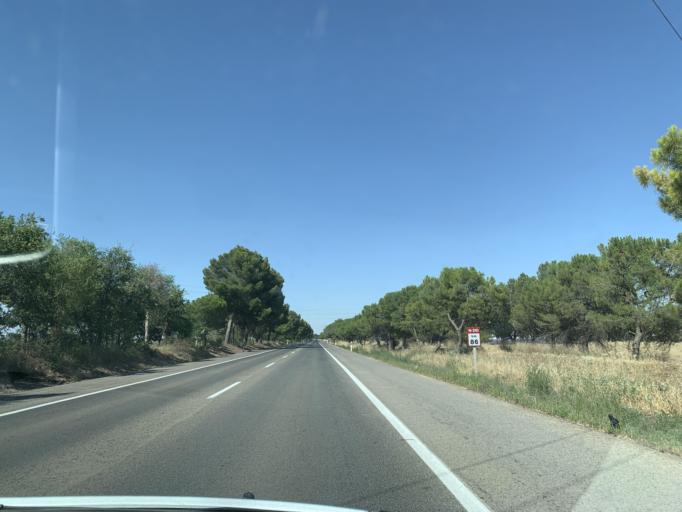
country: ES
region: Castille-La Mancha
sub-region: Provincia de Ciudad Real
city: Argamasilla de Alba
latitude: 39.1374
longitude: -3.0738
